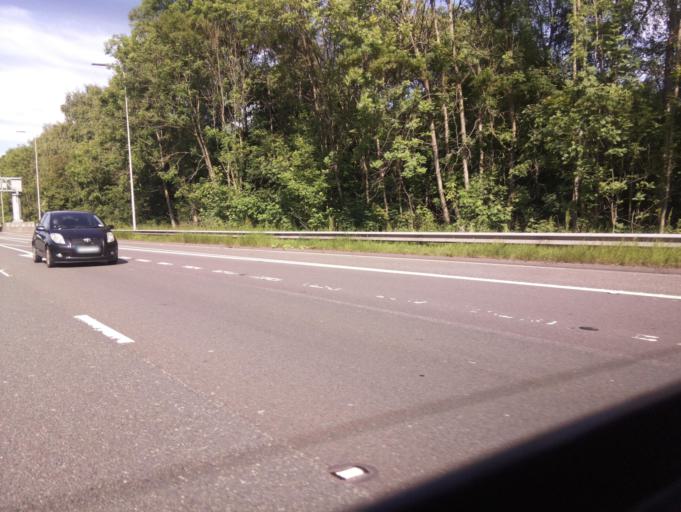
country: GB
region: England
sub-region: City and Borough of Salford
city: Walkden
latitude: 53.5057
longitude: -2.3777
